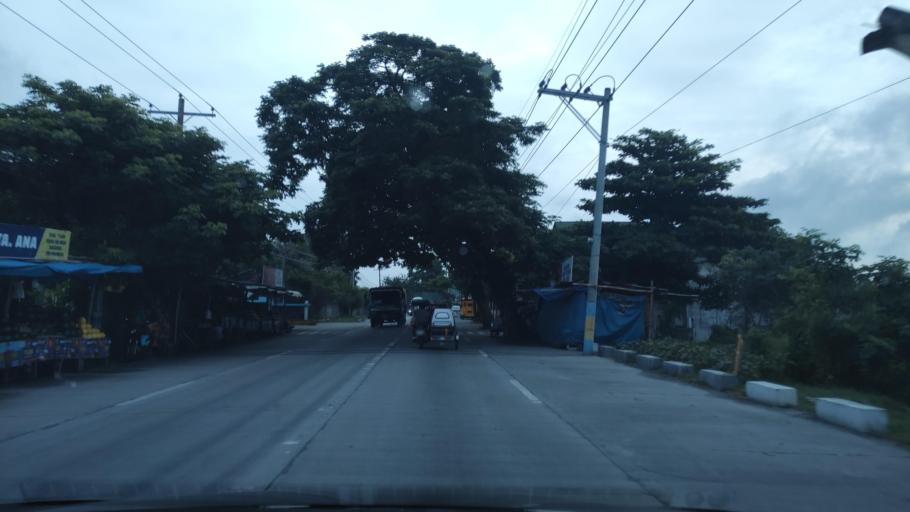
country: PH
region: Central Luzon
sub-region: Province of Pampanga
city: Santa Maria
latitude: 15.0859
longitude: 120.7649
